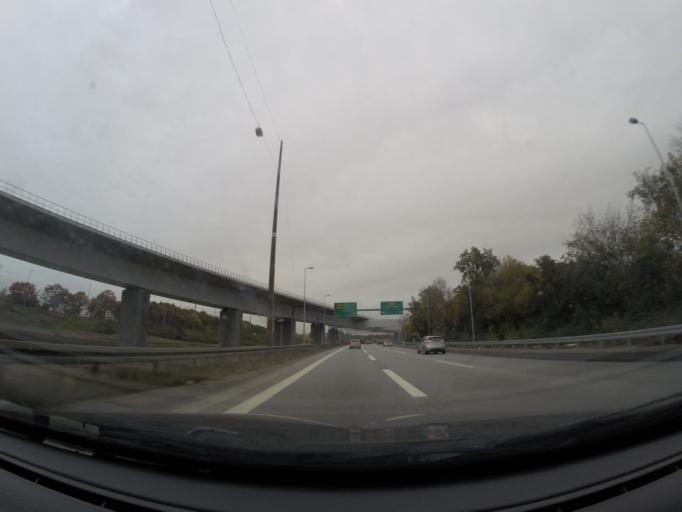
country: DK
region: Capital Region
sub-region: Ishoj Kommune
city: Ishoj
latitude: 55.6326
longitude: 12.3319
